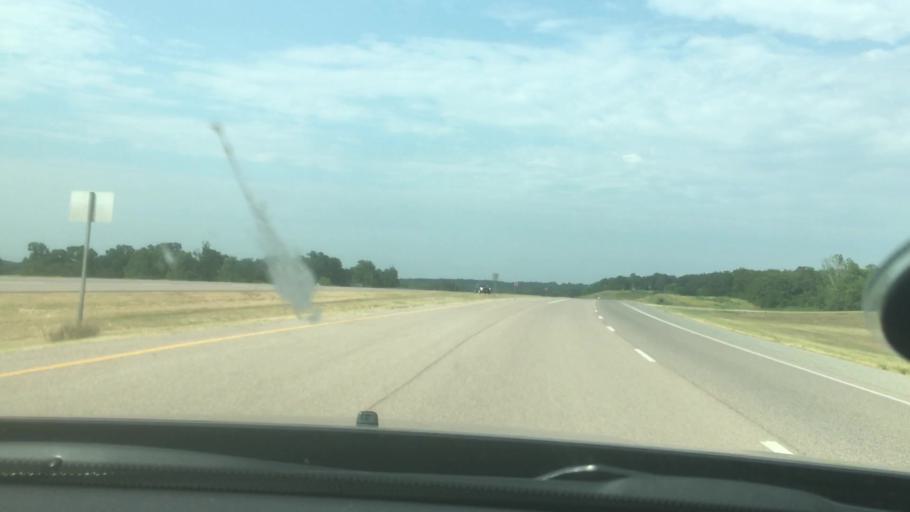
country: US
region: Oklahoma
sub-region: Pontotoc County
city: Byng
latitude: 34.8311
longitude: -96.6924
